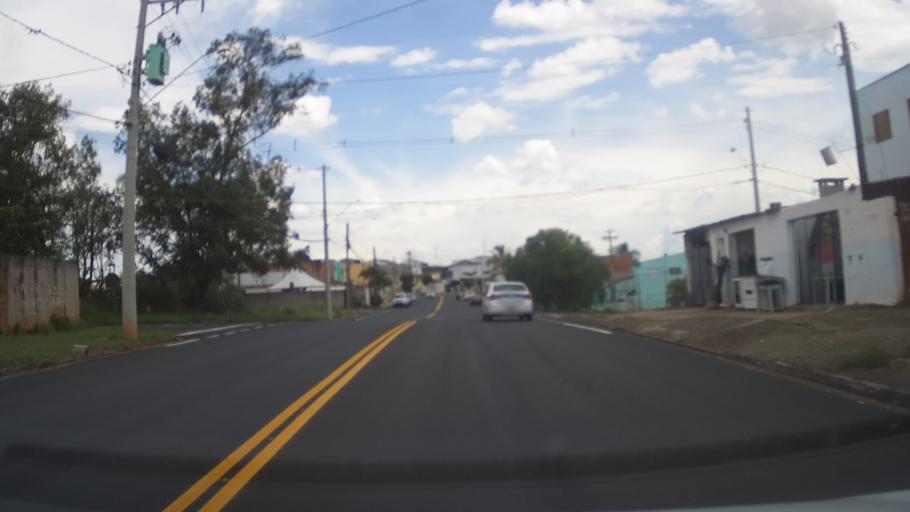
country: BR
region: Sao Paulo
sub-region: Campinas
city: Campinas
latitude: -22.9168
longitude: -47.0181
